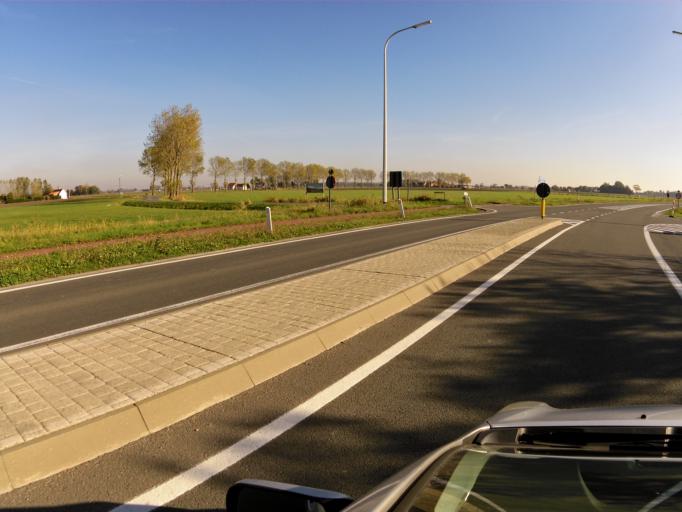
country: BE
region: Flanders
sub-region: Provincie West-Vlaanderen
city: Middelkerke
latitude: 51.1387
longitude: 2.8638
